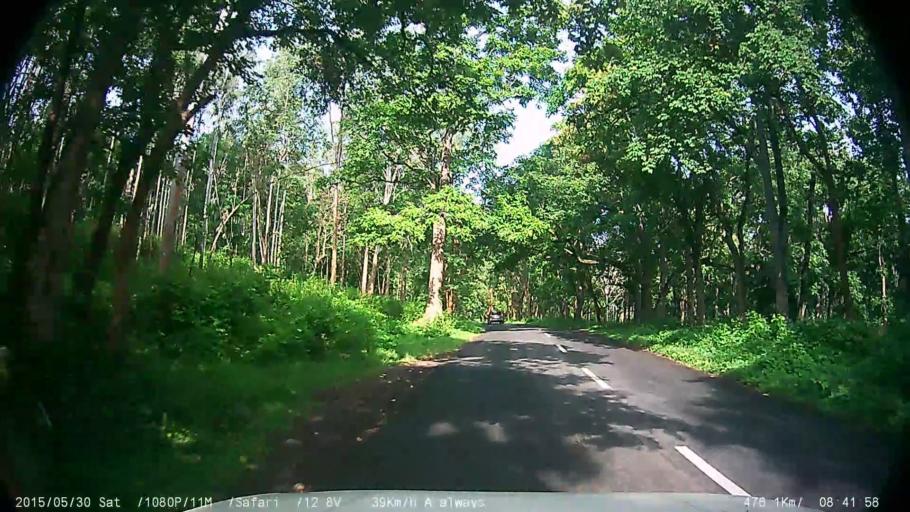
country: IN
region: Tamil Nadu
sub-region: Nilgiri
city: Naduvattam
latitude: 11.7053
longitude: 76.4070
